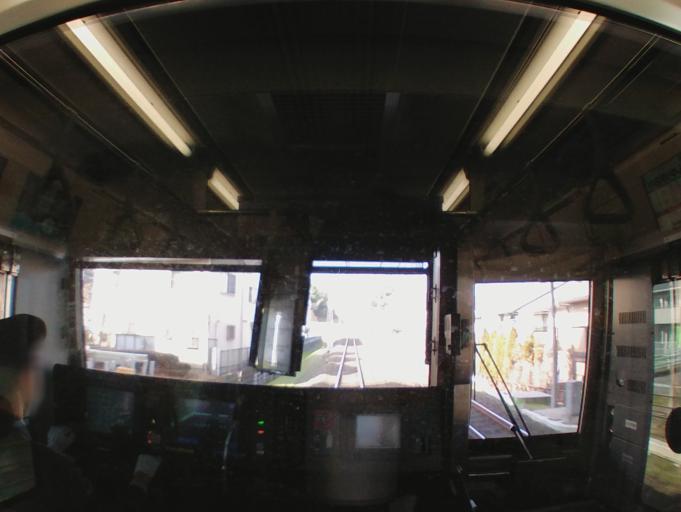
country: JP
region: Tokyo
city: Chofugaoka
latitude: 35.6156
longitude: 139.5574
